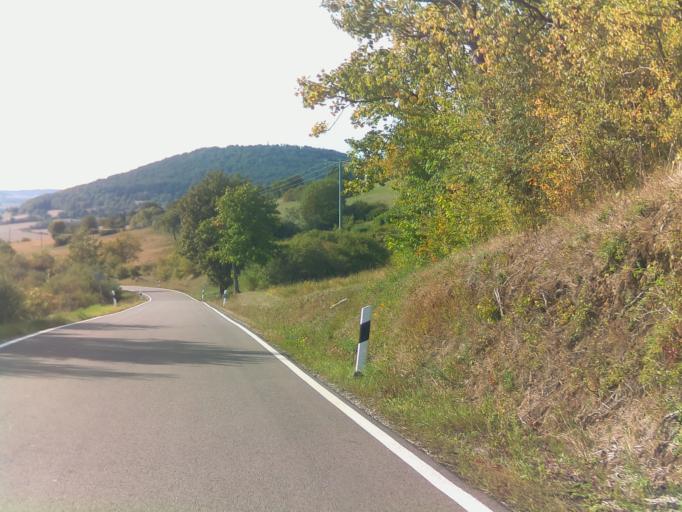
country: DE
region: Thuringia
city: Oberkatz
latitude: 50.5773
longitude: 10.2532
